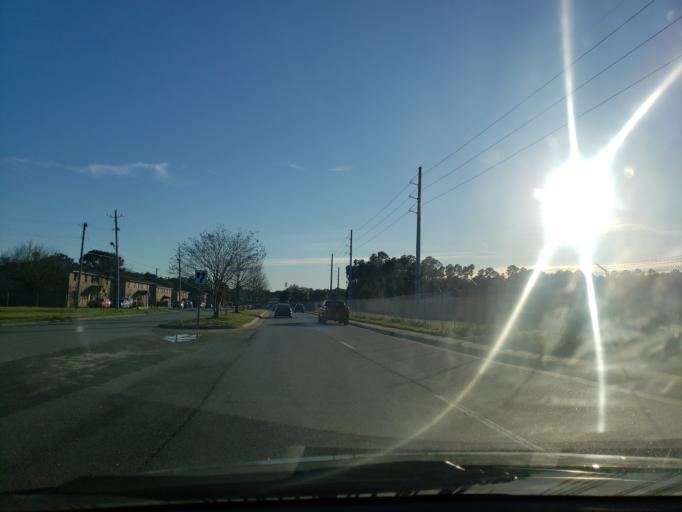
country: US
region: Georgia
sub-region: Chatham County
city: Montgomery
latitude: 32.0025
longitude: -81.1433
